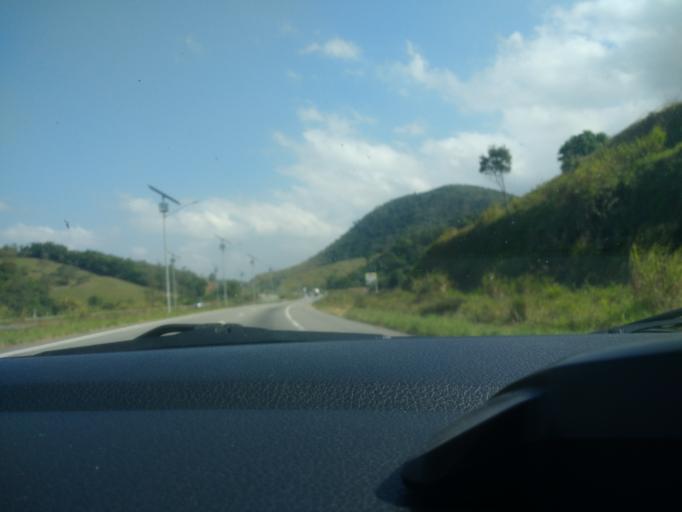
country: BR
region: Rio de Janeiro
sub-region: Queimados
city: Queimados
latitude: -22.6874
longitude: -43.4859
